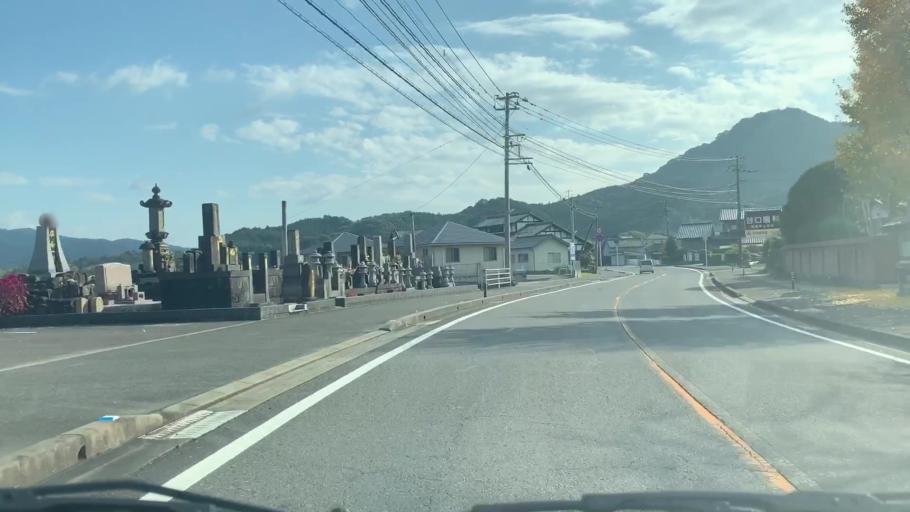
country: JP
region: Saga Prefecture
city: Takeocho-takeo
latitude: 33.1721
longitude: 130.0497
